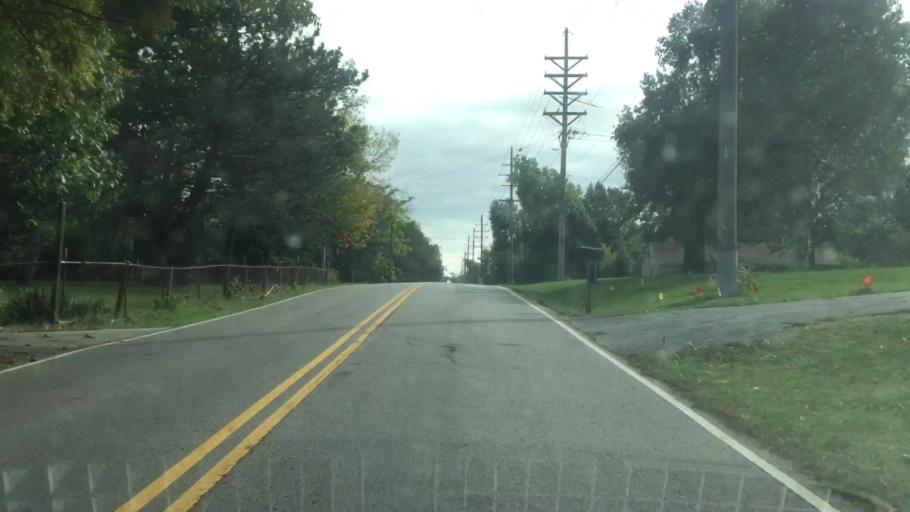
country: US
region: Kansas
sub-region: Johnson County
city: Shawnee
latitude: 39.0366
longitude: -94.7292
